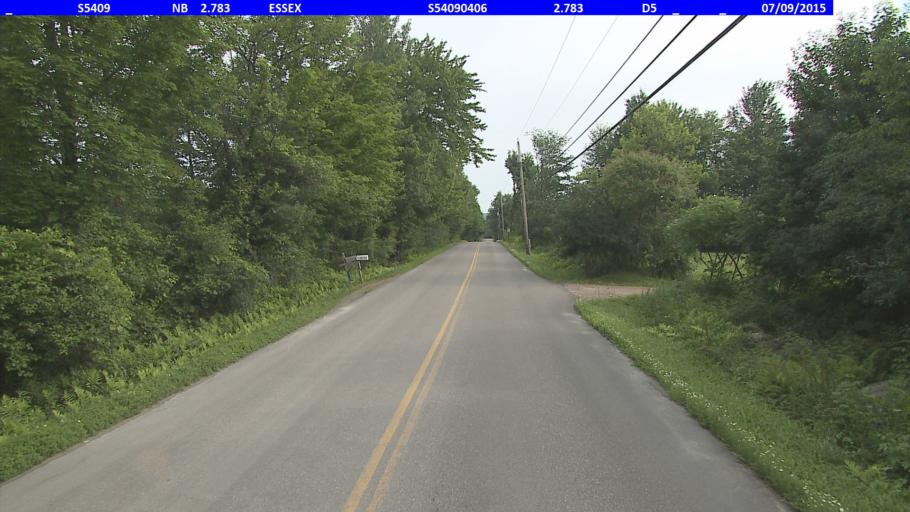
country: US
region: Vermont
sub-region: Chittenden County
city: Essex Junction
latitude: 44.5486
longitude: -73.0706
